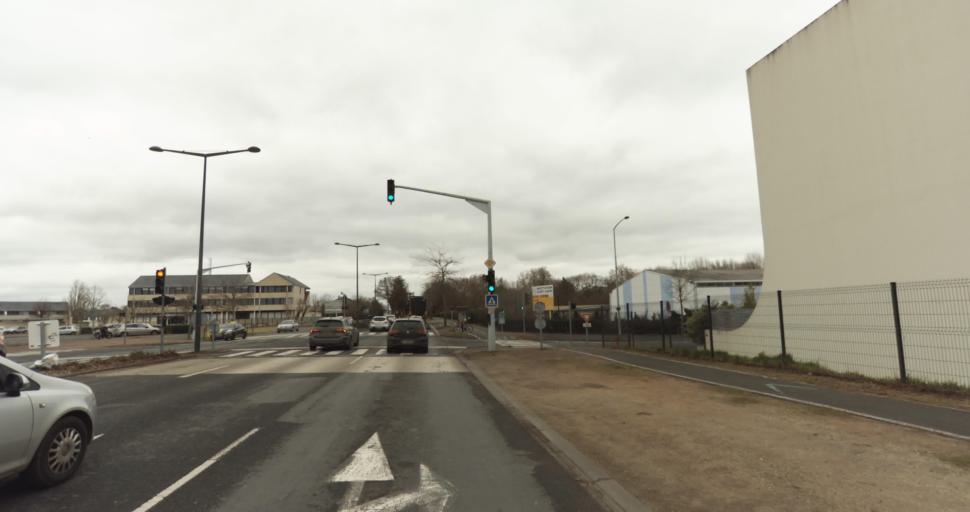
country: FR
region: Pays de la Loire
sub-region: Departement de Maine-et-Loire
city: Saumur
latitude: 47.2557
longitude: -0.0870
